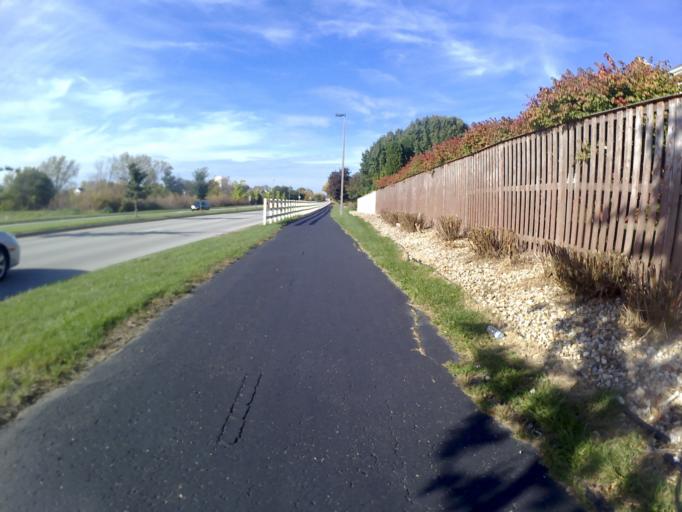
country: US
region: Illinois
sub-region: DuPage County
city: Woodridge
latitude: 41.7185
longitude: -88.0270
